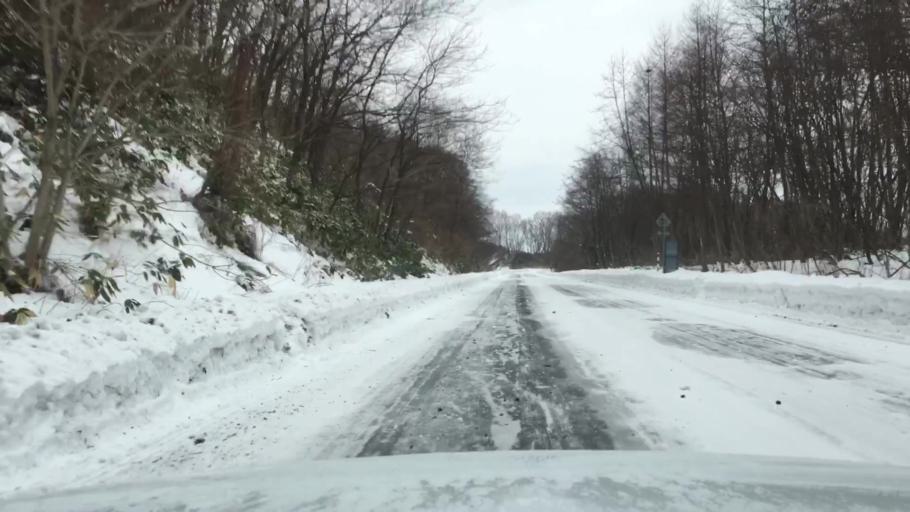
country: JP
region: Iwate
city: Shizukuishi
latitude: 39.9406
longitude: 140.9961
